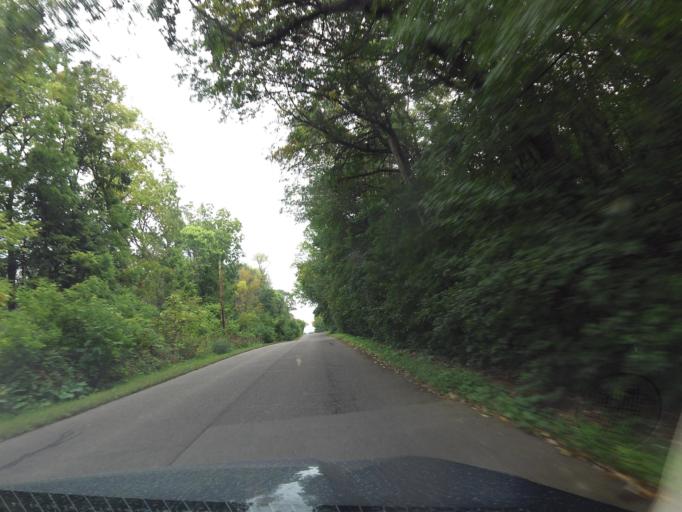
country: US
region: Minnesota
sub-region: Washington County
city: Afton
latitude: 44.8765
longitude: -92.8213
